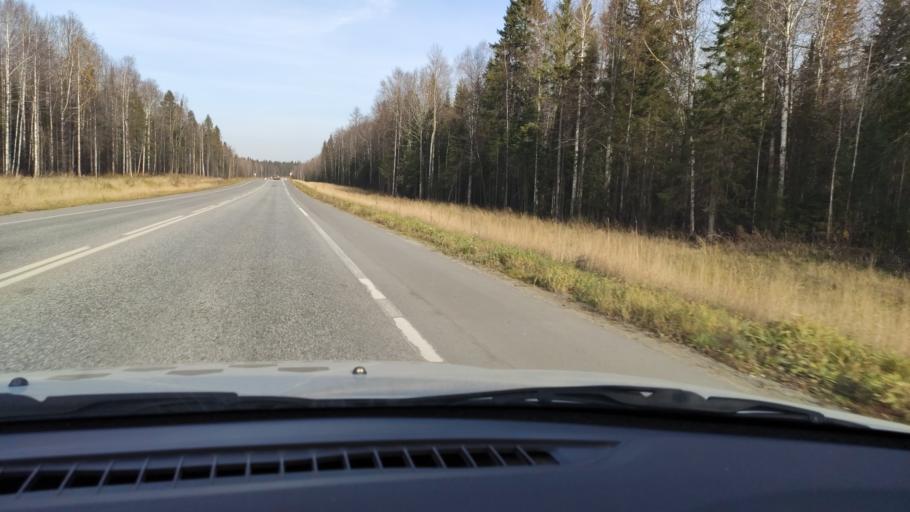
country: RU
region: Perm
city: Novyye Lyady
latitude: 58.0440
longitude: 56.5437
